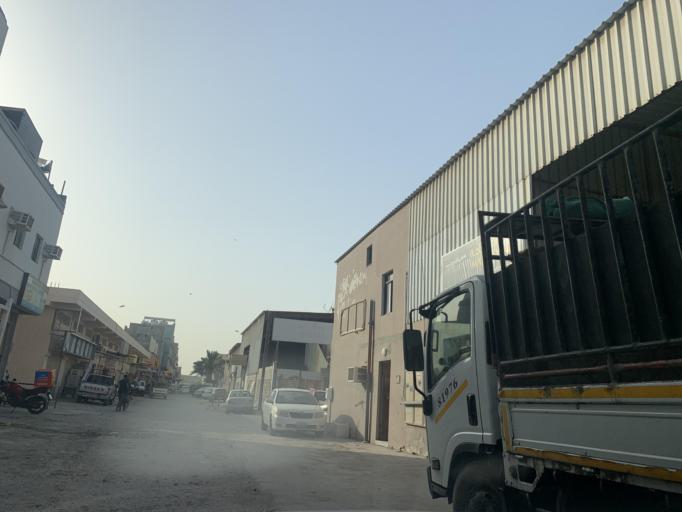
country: BH
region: Central Governorate
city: Madinat Hamad
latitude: 26.1451
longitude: 50.4870
